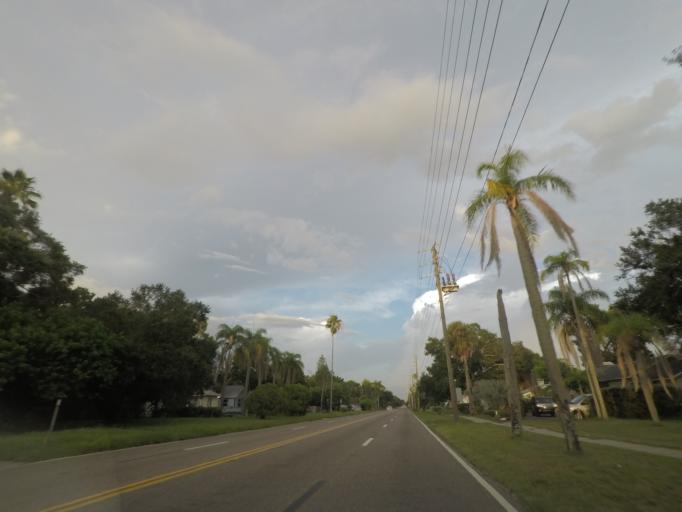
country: US
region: Florida
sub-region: Pinellas County
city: Gulfport
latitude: 27.7483
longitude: -82.6951
